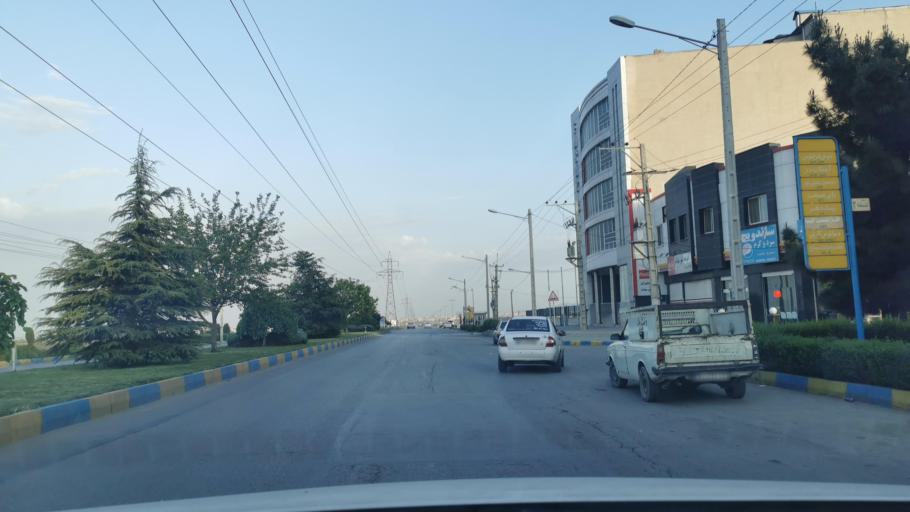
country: IR
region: Razavi Khorasan
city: Torqabeh
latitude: 36.4229
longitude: 59.4261
